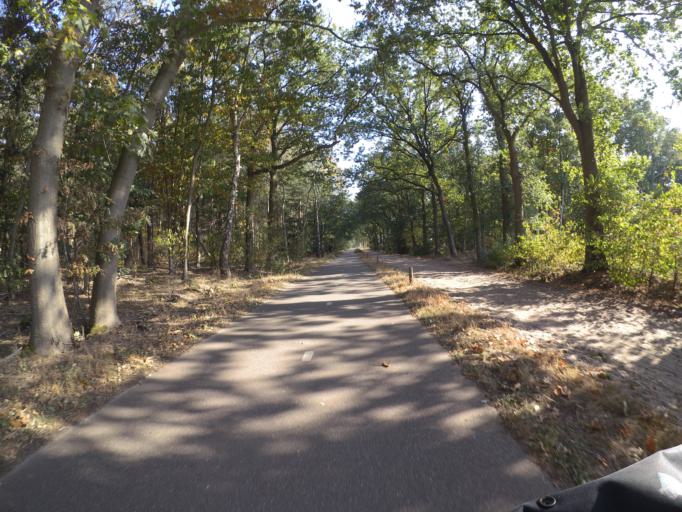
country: NL
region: North Brabant
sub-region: Gemeente Oirschot
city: Oostelbeers
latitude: 51.4745
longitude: 5.2853
